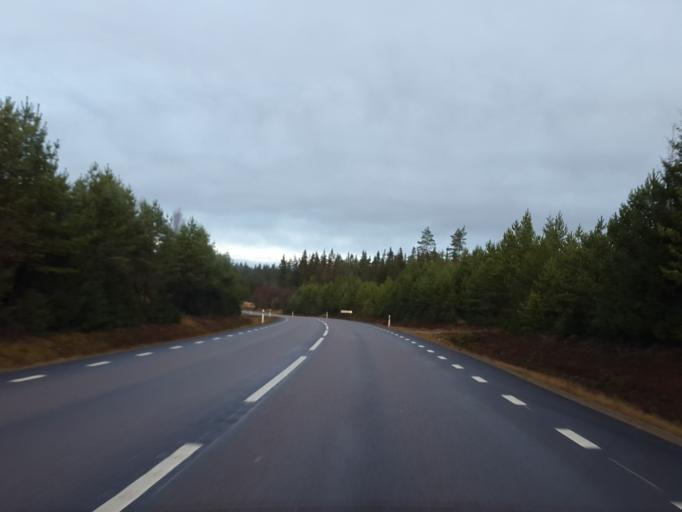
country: SE
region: Vaestra Goetaland
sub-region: Boras Kommun
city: Sandared
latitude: 57.7925
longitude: 12.7692
